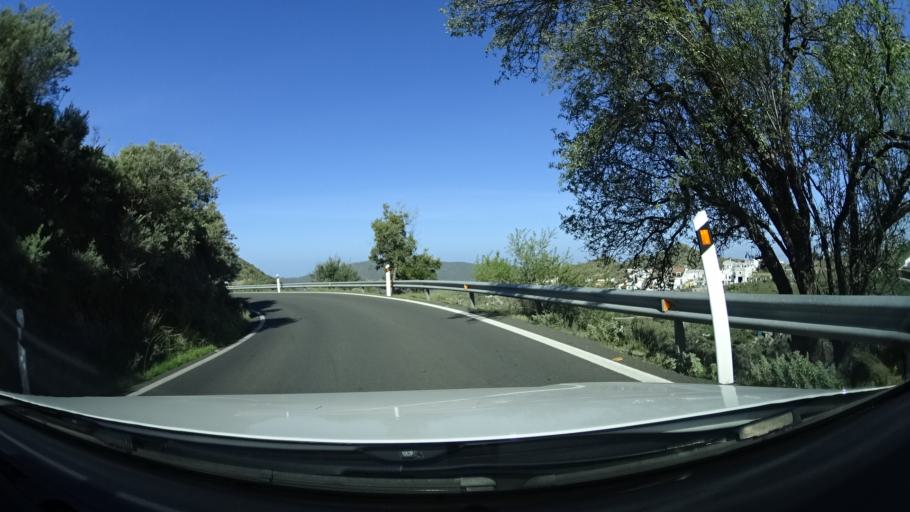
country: ES
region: Canary Islands
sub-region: Provincia de Las Palmas
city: Artenara
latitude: 28.0242
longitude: -15.6356
